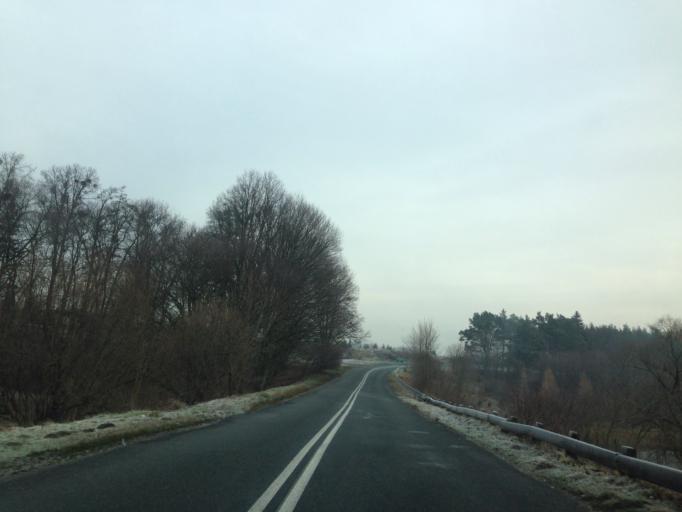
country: PL
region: Kujawsko-Pomorskie
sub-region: Powiat brodnicki
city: Gorzno
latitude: 53.2441
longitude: 19.6657
